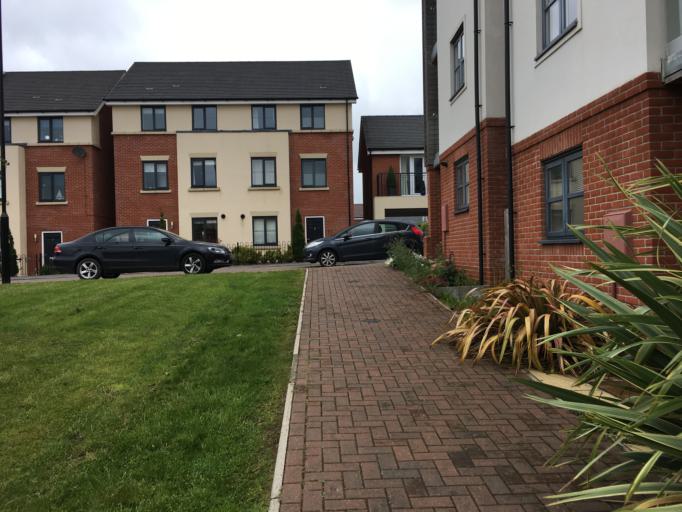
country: GB
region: England
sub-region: Warwickshire
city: Rugby
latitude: 52.3970
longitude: -1.2508
